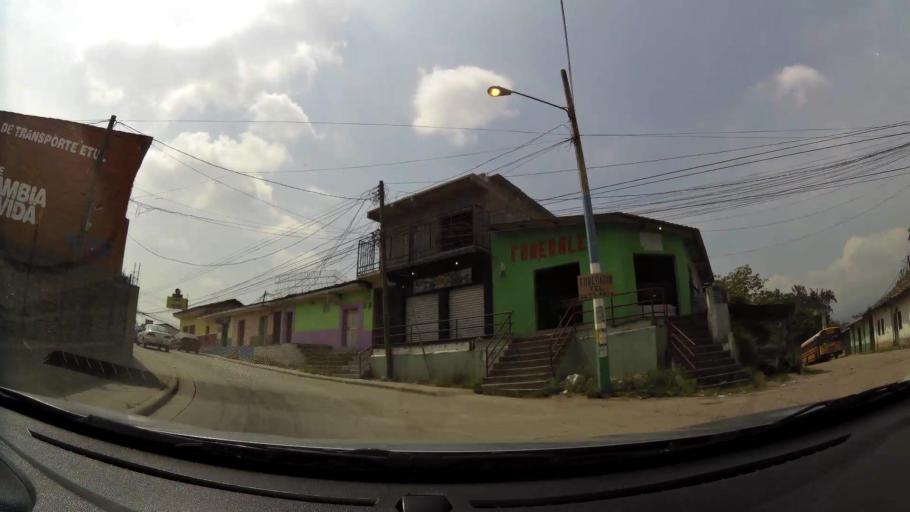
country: HN
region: Comayagua
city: Siguatepeque
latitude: 14.5967
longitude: -87.8329
